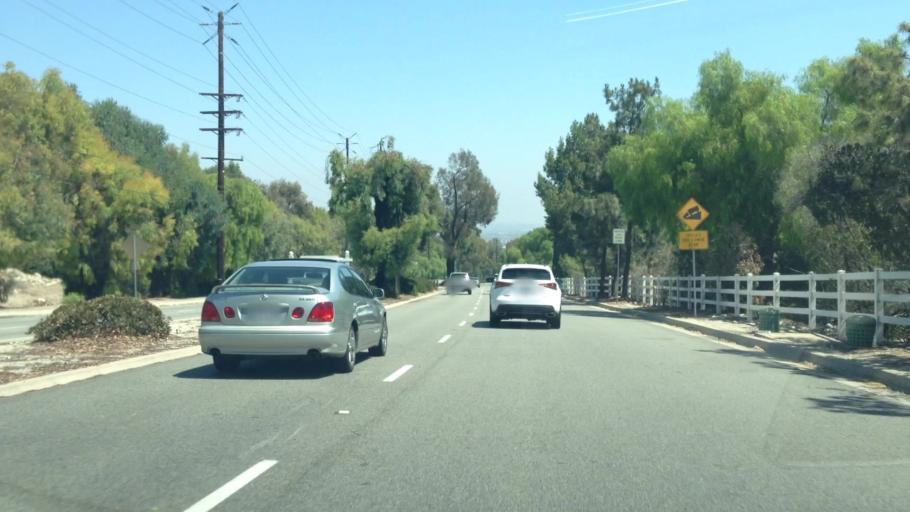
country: US
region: California
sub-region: Los Angeles County
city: Rolling Hills Estates
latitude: 33.7885
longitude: -118.3571
